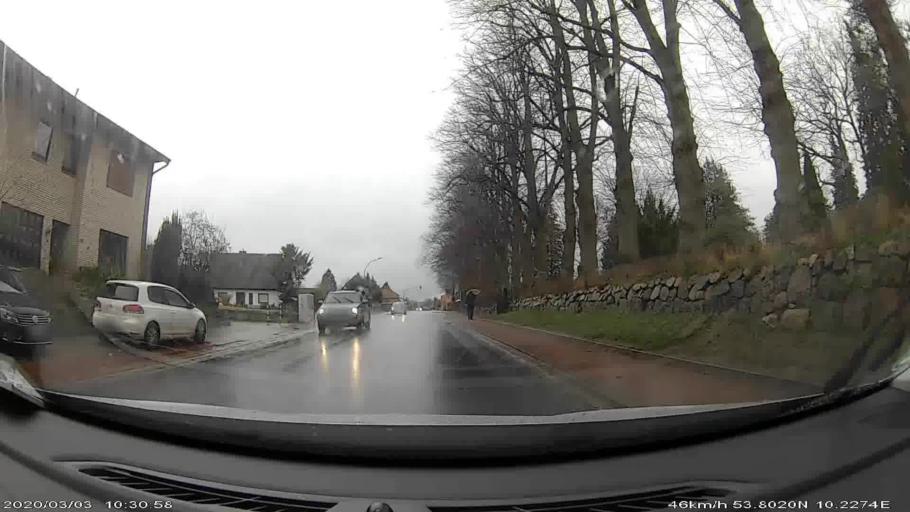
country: DE
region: Schleswig-Holstein
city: Sulfeld
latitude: 53.8032
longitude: 10.2238
